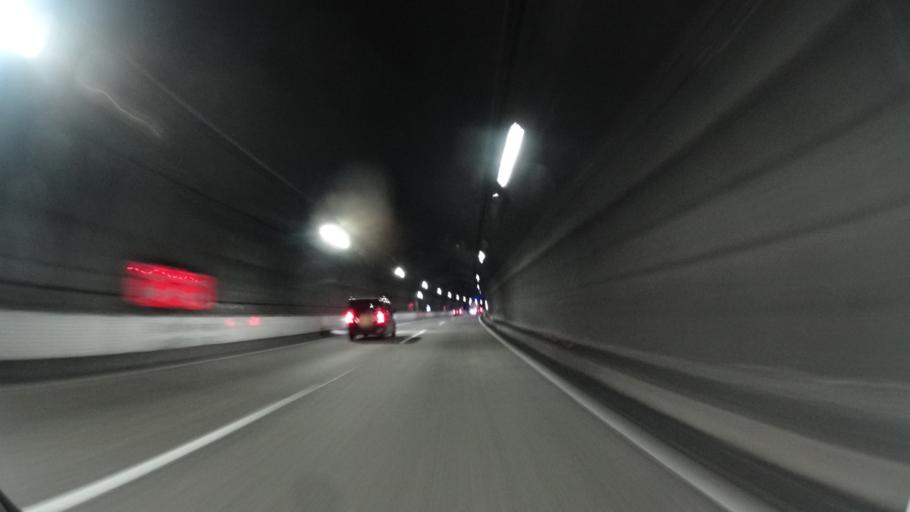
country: JP
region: Okayama
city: Okayama-shi
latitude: 34.7870
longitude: 134.1400
